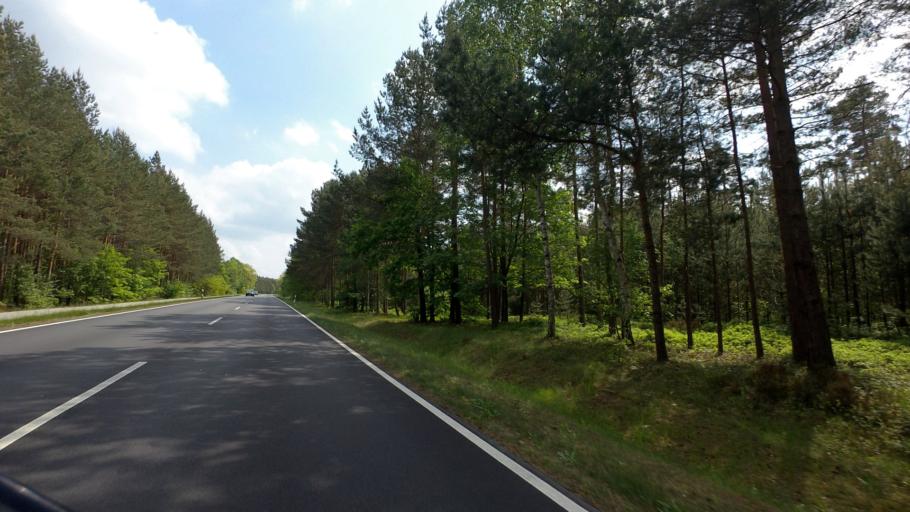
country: DE
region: Saxony
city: Niesky
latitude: 51.3233
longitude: 14.8226
